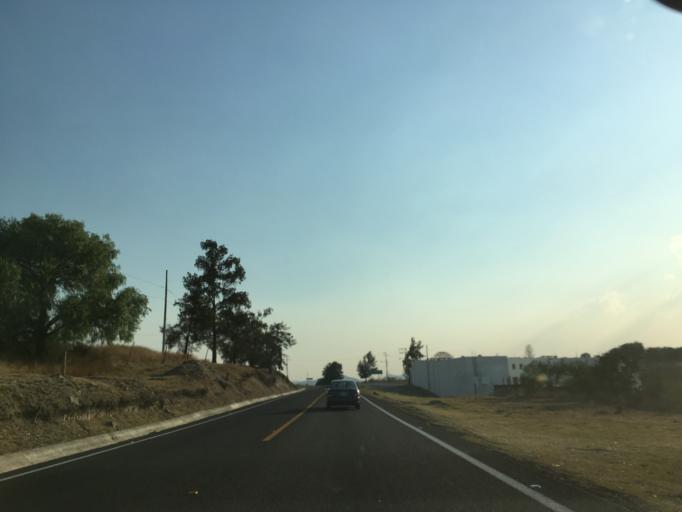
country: MX
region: Michoacan
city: Charo
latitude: 19.7603
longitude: -101.0334
